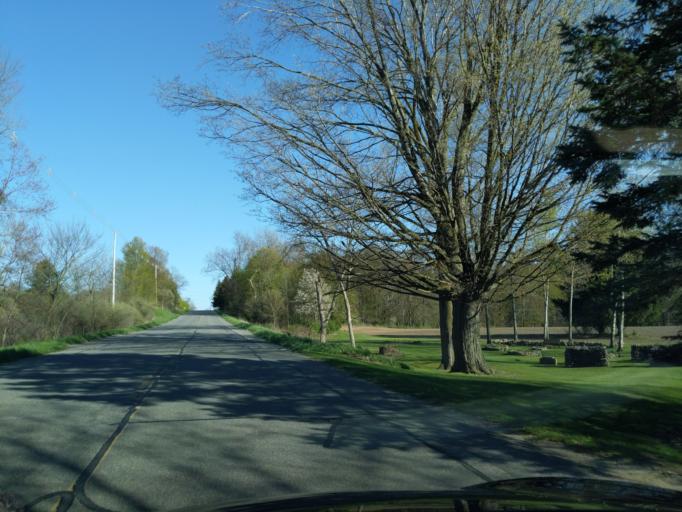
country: US
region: Michigan
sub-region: Ionia County
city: Portland
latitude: 42.8385
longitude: -84.8610
